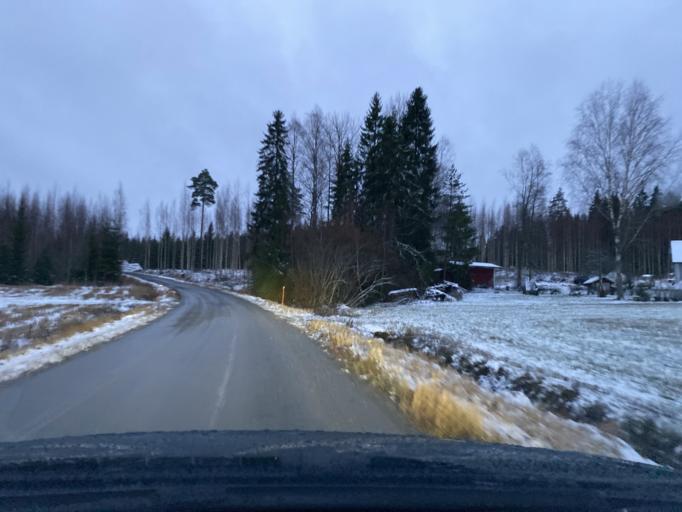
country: FI
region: Pirkanmaa
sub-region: Lounais-Pirkanmaa
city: Punkalaidun
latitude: 61.1592
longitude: 22.9597
